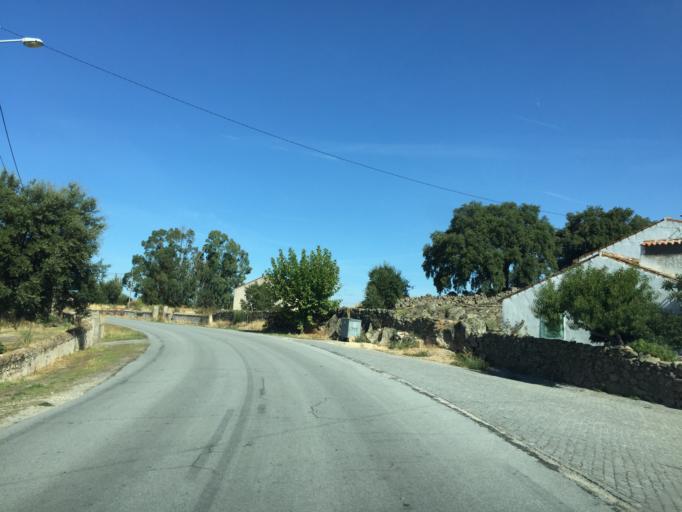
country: PT
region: Portalegre
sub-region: Marvao
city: Marvao
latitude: 39.4391
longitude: -7.3653
